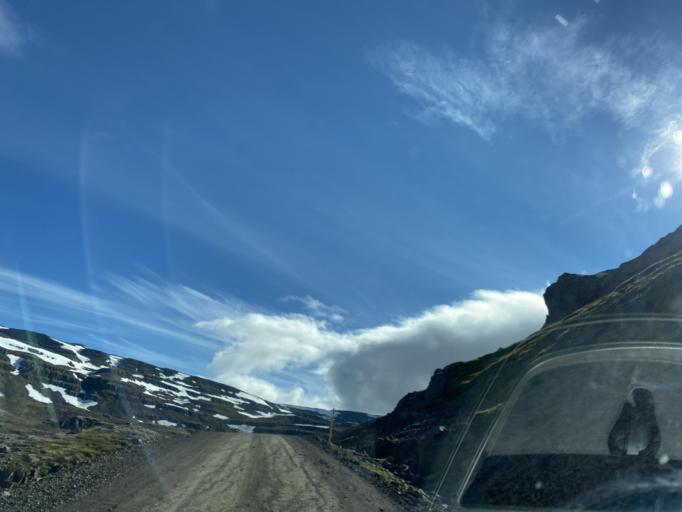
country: IS
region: East
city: Eskifjoerdur
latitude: 65.1747
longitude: -14.1147
